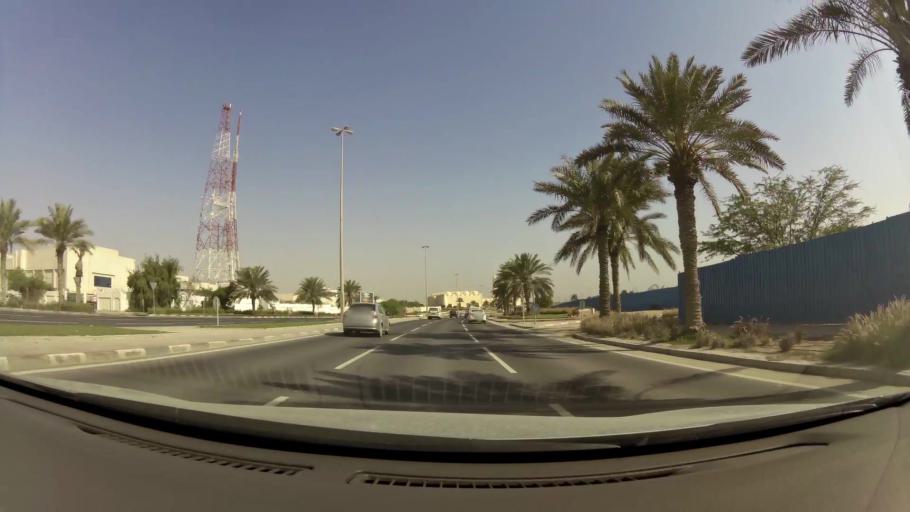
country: QA
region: Baladiyat ad Dawhah
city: Doha
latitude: 25.3098
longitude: 51.5048
